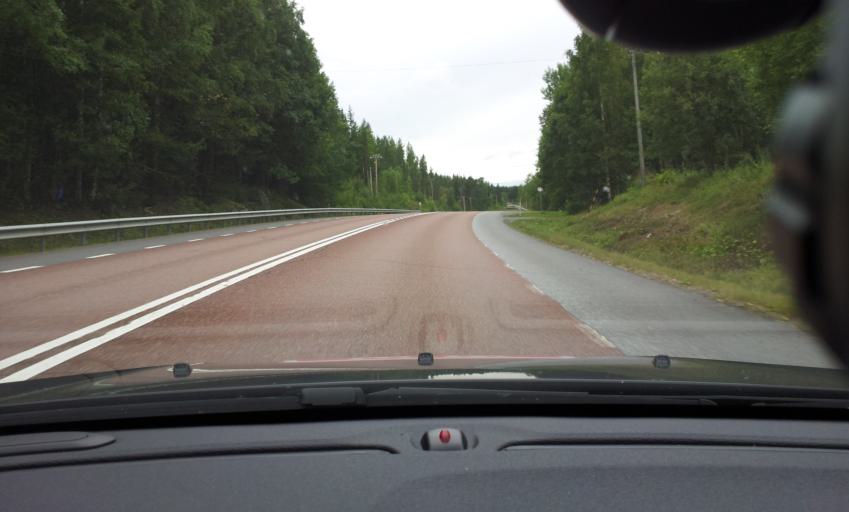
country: SE
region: Jaemtland
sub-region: Braecke Kommun
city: Braecke
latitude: 62.9531
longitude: 15.1502
